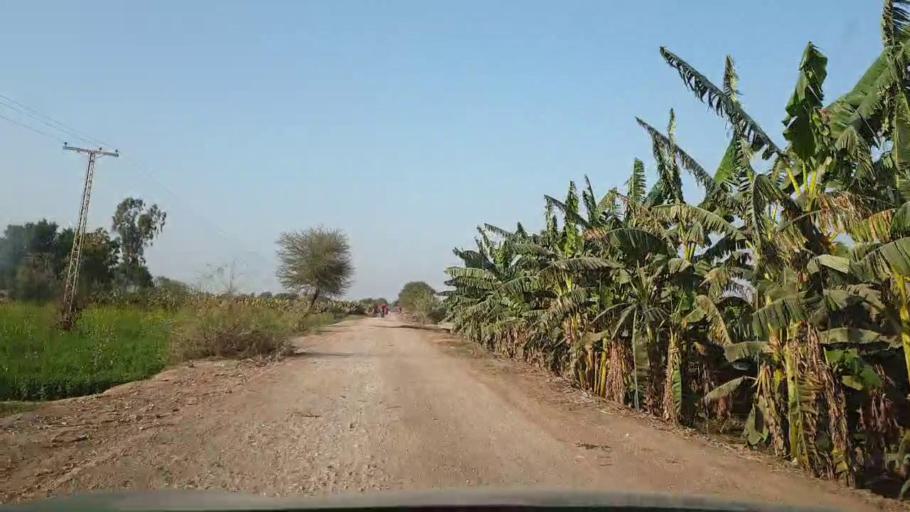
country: PK
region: Sindh
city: Tando Allahyar
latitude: 25.5781
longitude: 68.7801
